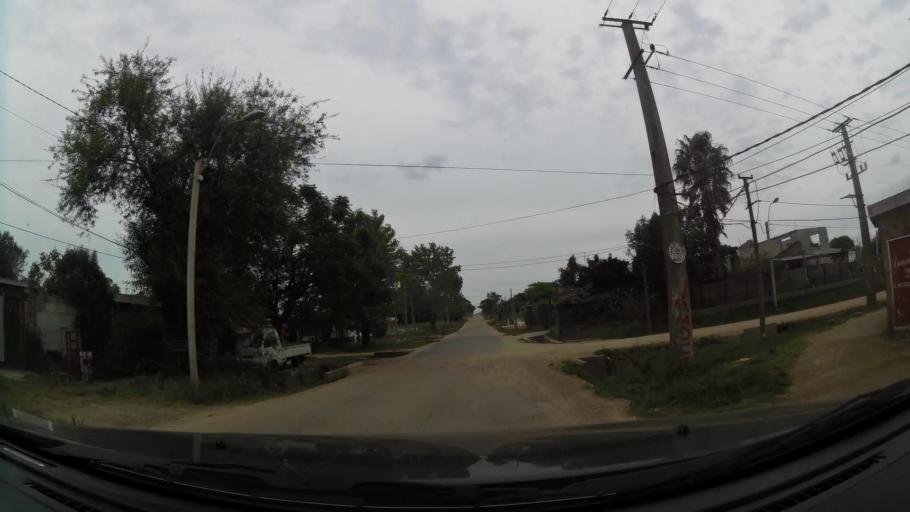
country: UY
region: Canelones
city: Las Piedras
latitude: -34.7179
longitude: -56.2030
